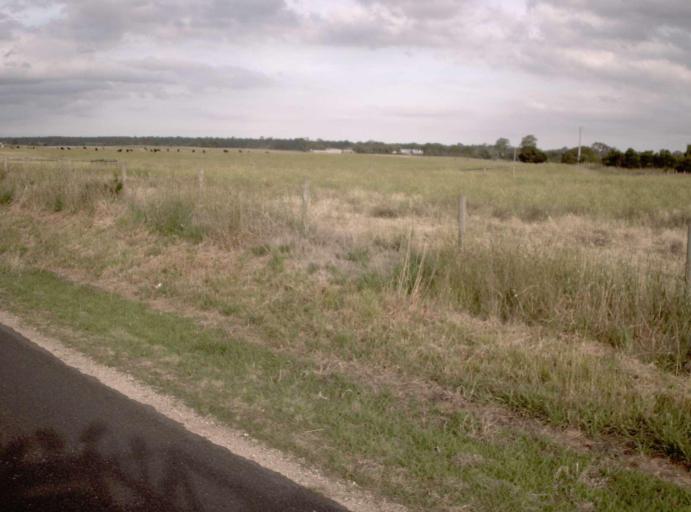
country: AU
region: Victoria
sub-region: Wellington
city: Sale
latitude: -37.8644
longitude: 147.0306
